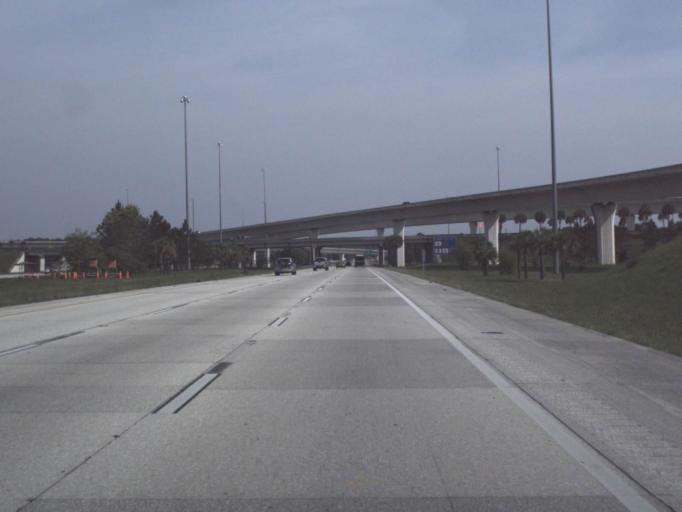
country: US
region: Florida
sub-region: Saint Johns County
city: Fruit Cove
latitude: 30.1636
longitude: -81.5531
